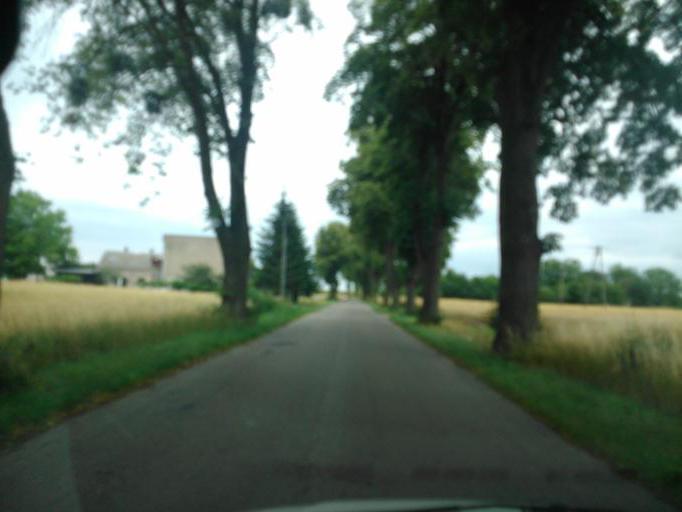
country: PL
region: Kujawsko-Pomorskie
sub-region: Powiat brodnicki
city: Brodnica
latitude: 53.2552
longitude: 19.3552
